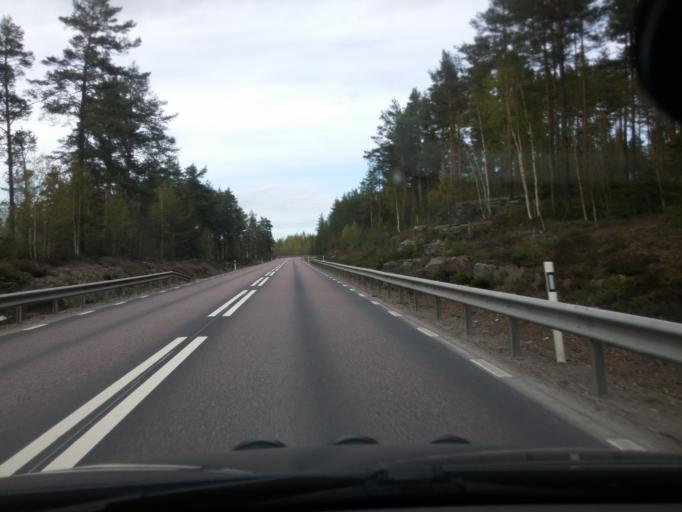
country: SE
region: Gaevleborg
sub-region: Ljusdals Kommun
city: Ljusdal
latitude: 61.8210
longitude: 16.0270
